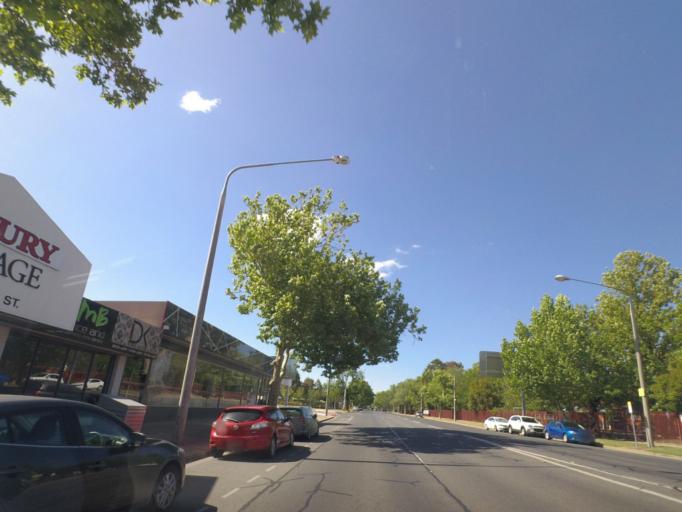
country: AU
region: New South Wales
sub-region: Albury Municipality
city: Albury
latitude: -36.0740
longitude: 146.9255
